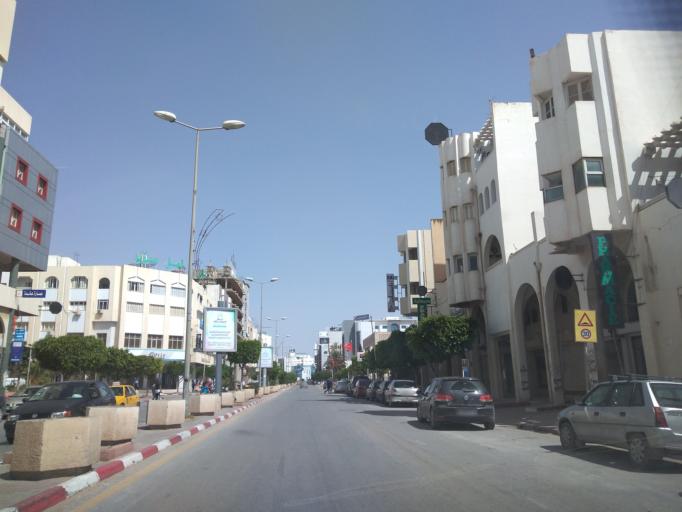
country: TN
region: Safaqis
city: Sfax
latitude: 34.7377
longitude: 10.7554
